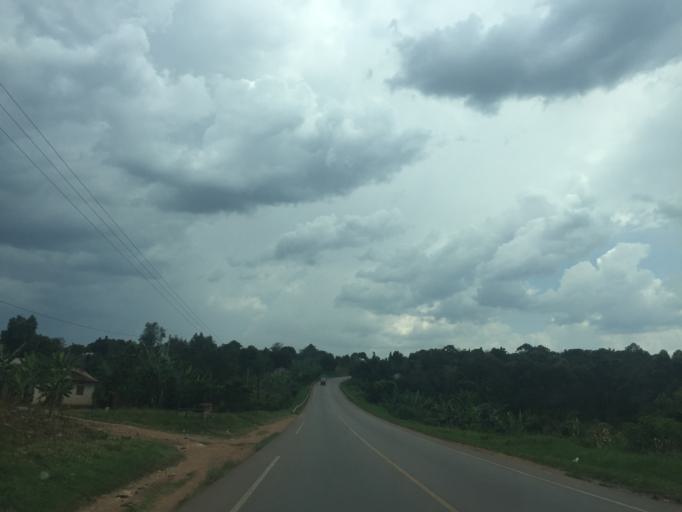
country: UG
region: Central Region
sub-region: Luwero District
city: Wobulenzi
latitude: 0.6758
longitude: 32.5272
